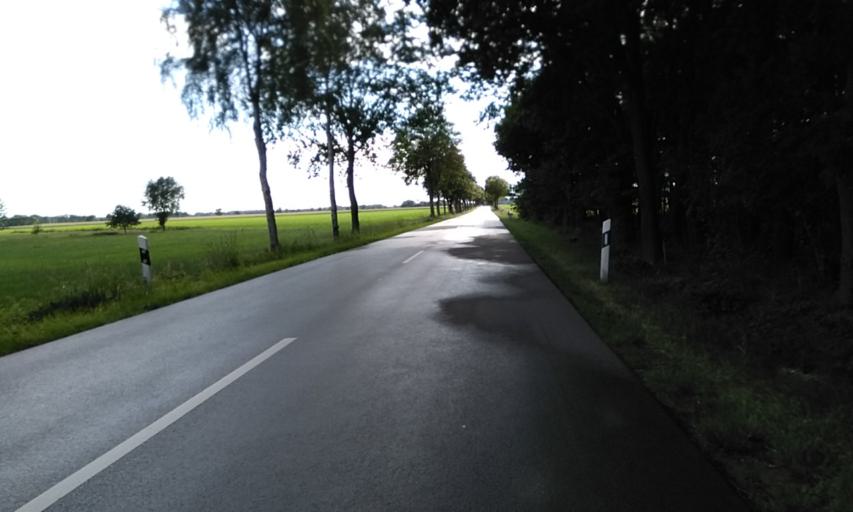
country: DE
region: Lower Saxony
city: Vierden
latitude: 53.3566
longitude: 9.4976
